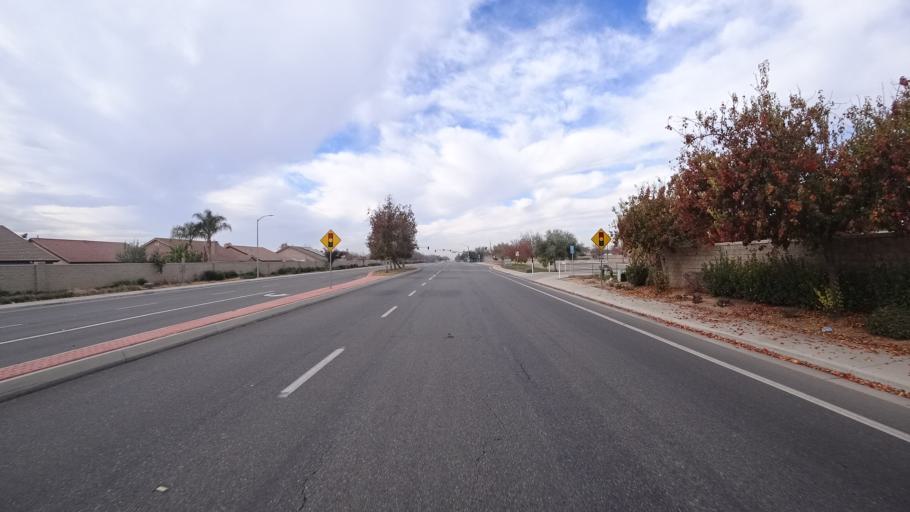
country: US
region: California
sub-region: Kern County
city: Rosedale
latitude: 35.4198
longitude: -119.1346
